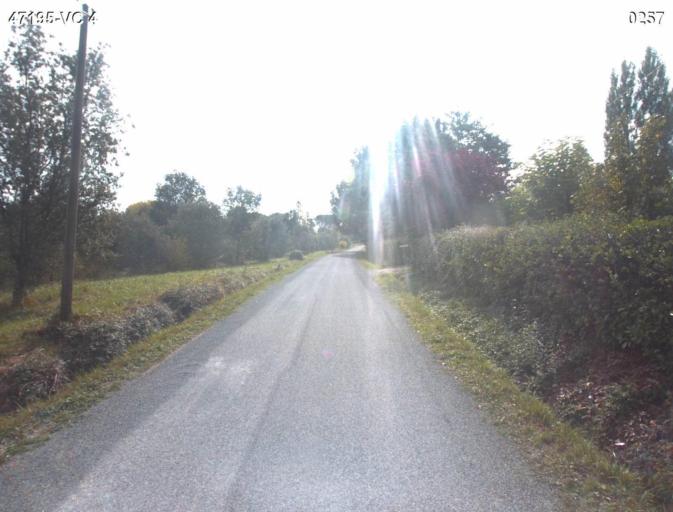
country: FR
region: Aquitaine
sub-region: Departement du Lot-et-Garonne
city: Nerac
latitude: 44.1185
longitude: 0.3769
